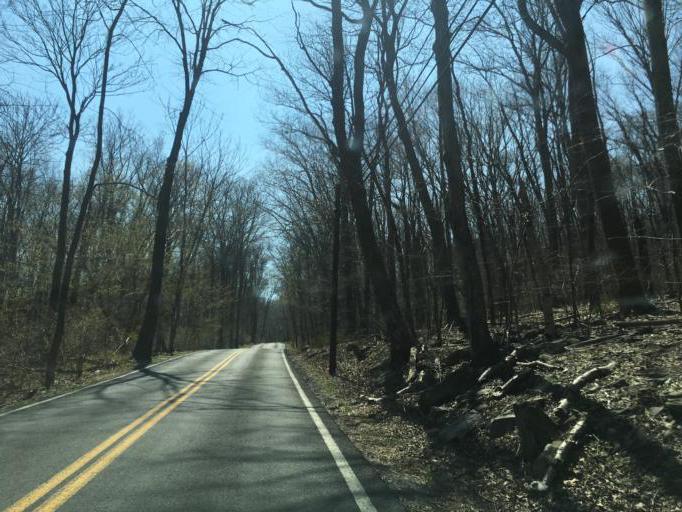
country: US
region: Maryland
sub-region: Washington County
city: Smithsburg
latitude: 39.6310
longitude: -77.5586
